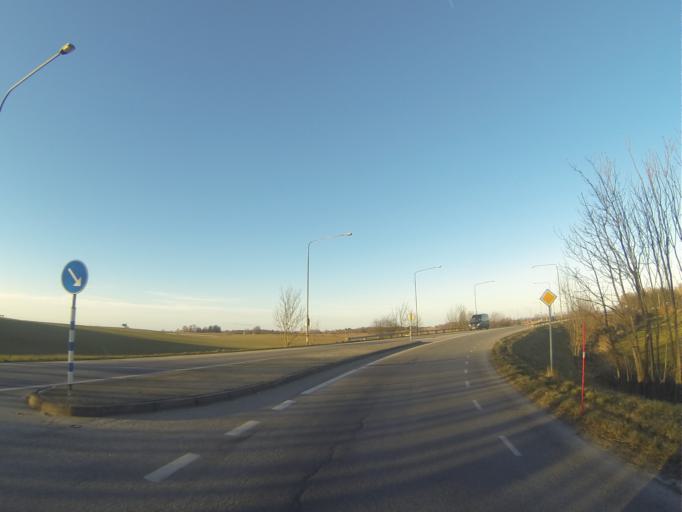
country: SE
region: Skane
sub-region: Malmo
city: Oxie
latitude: 55.5525
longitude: 13.0950
